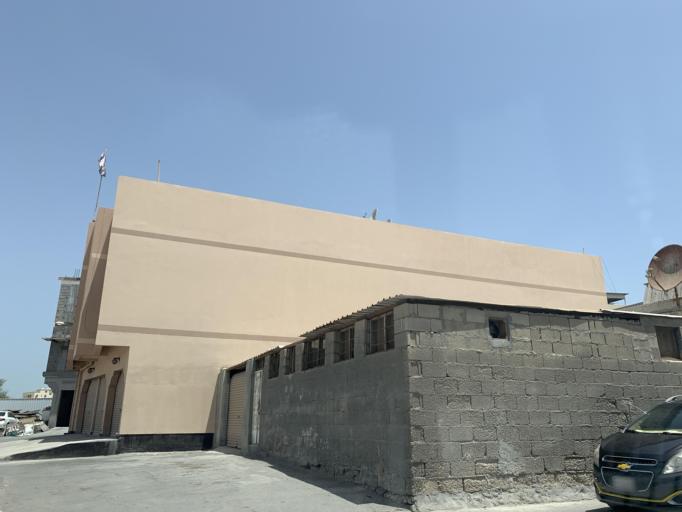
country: BH
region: Northern
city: Sitrah
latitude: 26.1724
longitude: 50.6086
